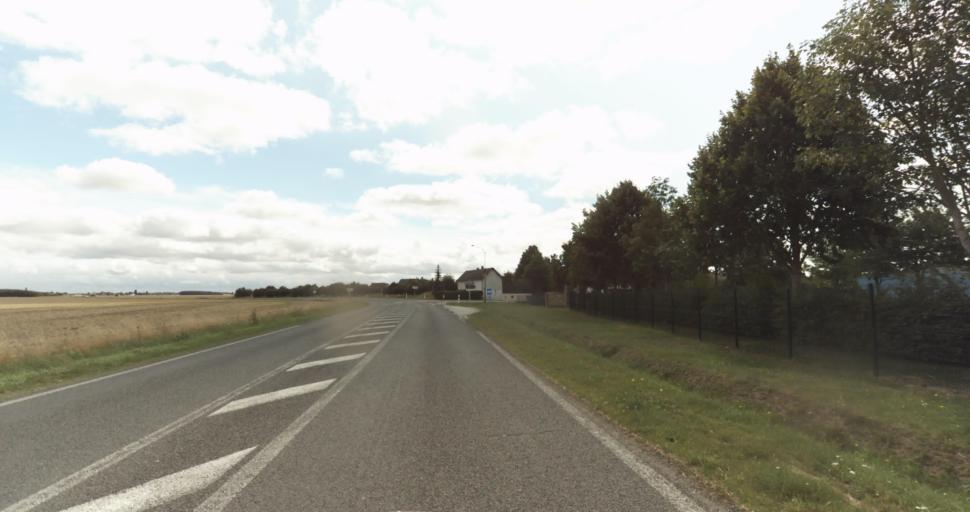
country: FR
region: Haute-Normandie
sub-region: Departement de l'Eure
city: Evreux
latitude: 48.9779
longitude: 1.1927
